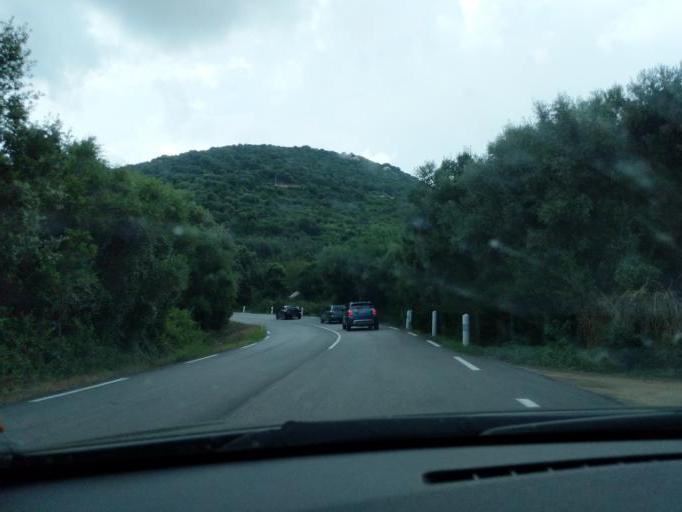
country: FR
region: Corsica
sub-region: Departement de la Corse-du-Sud
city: Sartene
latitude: 41.5799
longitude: 8.9481
